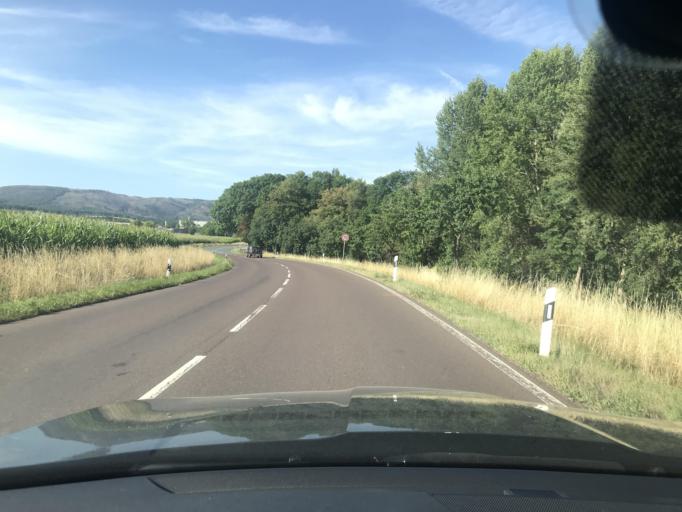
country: DE
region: Saxony-Anhalt
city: Drubeck
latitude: 51.8844
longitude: 10.7082
